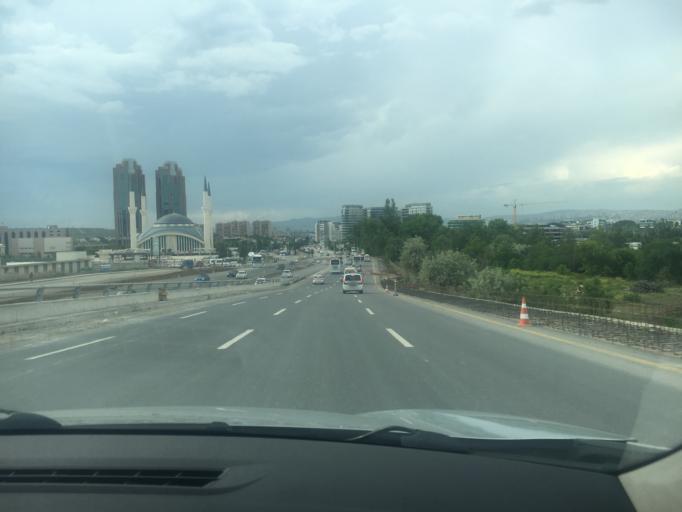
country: TR
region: Ankara
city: Batikent
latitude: 39.9022
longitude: 32.7657
